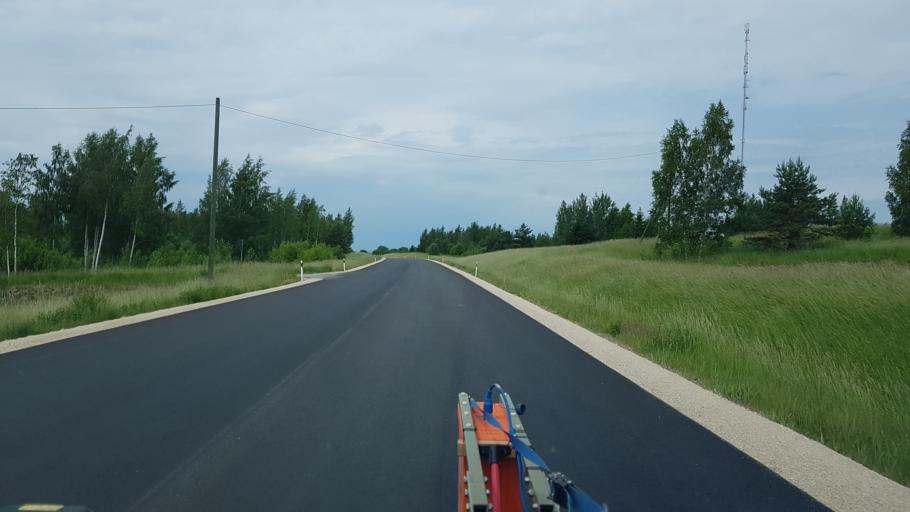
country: EE
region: Vorumaa
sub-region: Voru linn
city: Voru
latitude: 57.7458
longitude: 27.2488
